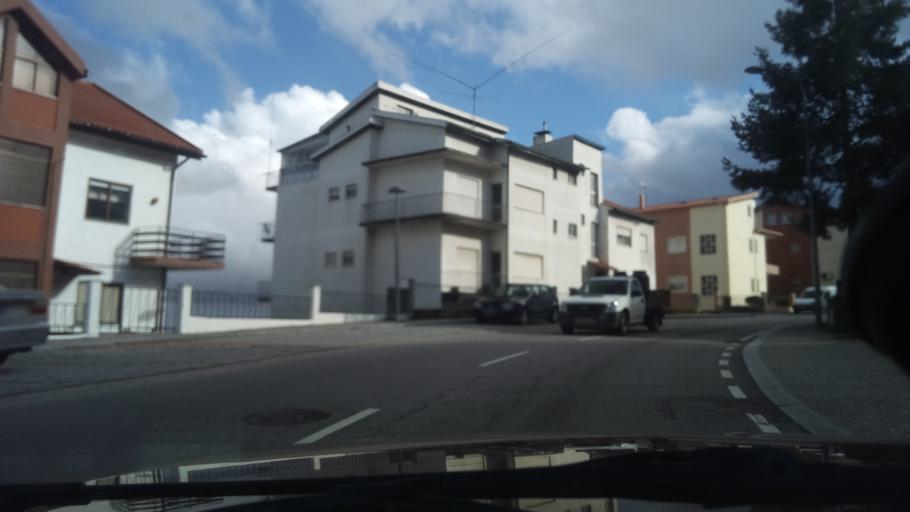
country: PT
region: Guarda
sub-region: Guarda
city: Guarda
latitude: 40.5377
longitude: -7.2618
